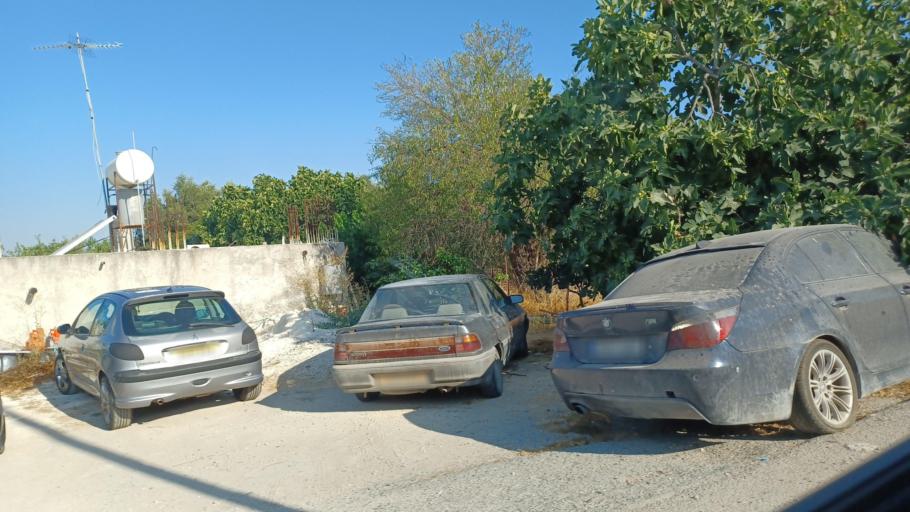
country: CY
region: Pafos
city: Mesogi
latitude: 34.8882
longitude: 32.5095
